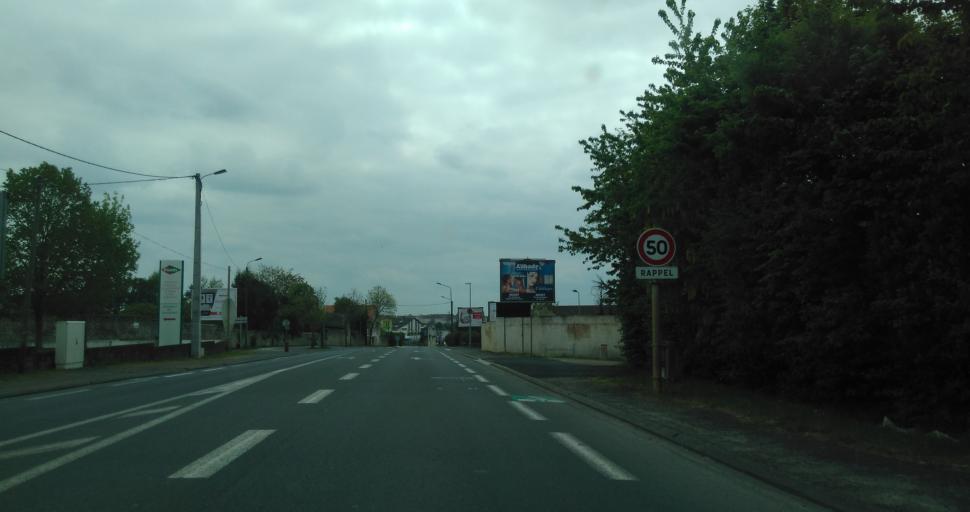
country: FR
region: Poitou-Charentes
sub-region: Departement des Deux-Sevres
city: Niort
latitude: 46.3433
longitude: -0.4446
